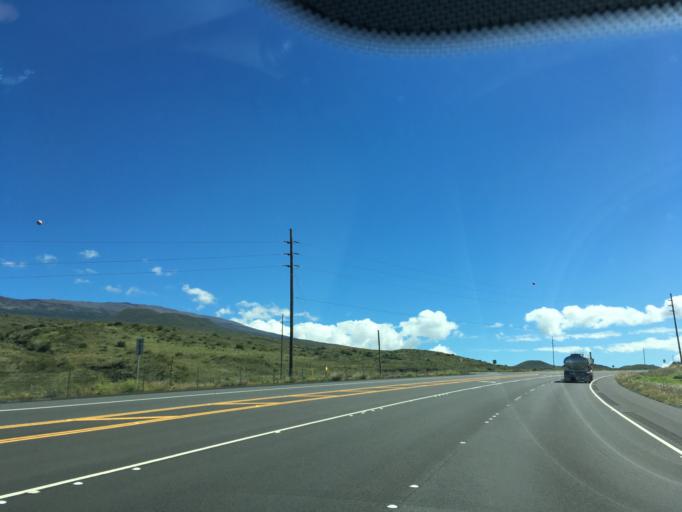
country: US
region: Hawaii
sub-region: Hawaii County
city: Waikoloa
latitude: 19.7928
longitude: -155.6274
